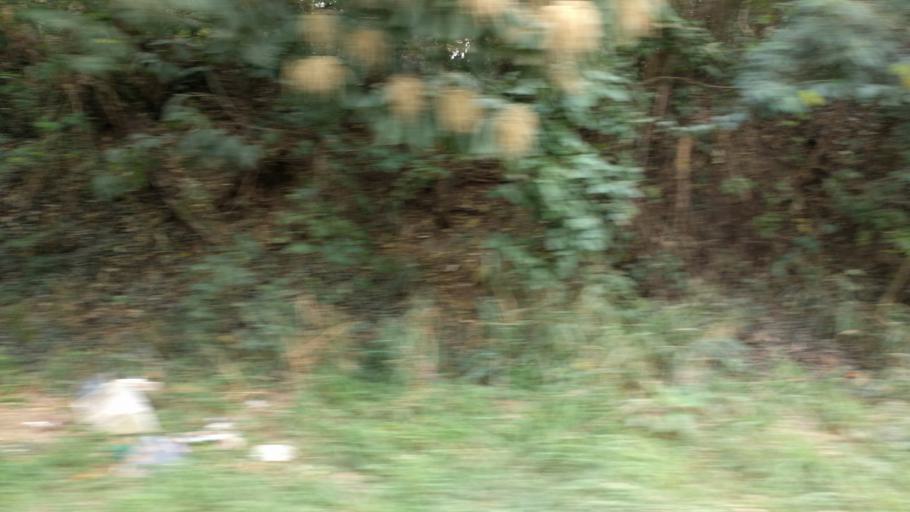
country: BO
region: Santa Cruz
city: Santa Rita
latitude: -17.9246
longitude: -63.3461
